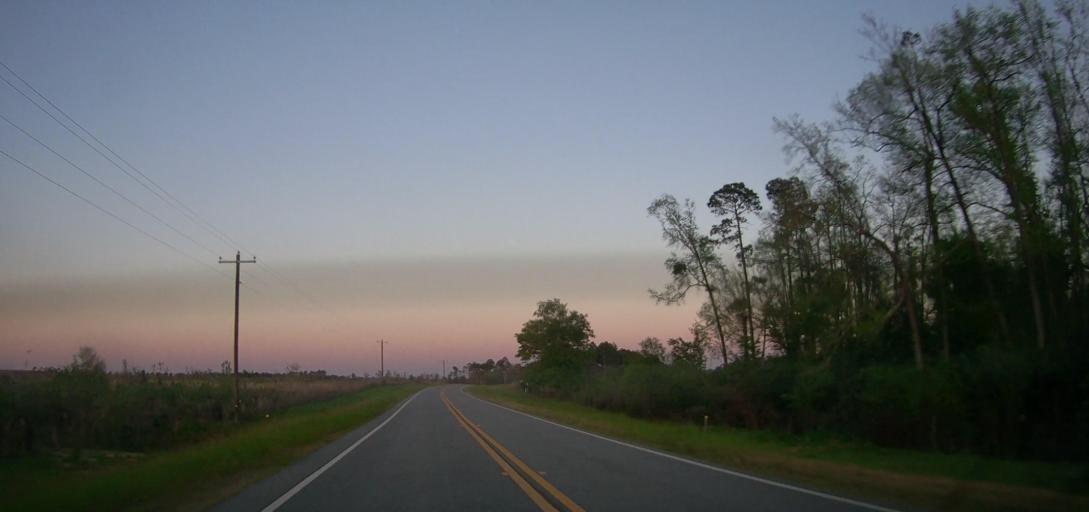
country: US
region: Georgia
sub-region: Turner County
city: Ashburn
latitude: 31.8240
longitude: -83.5513
